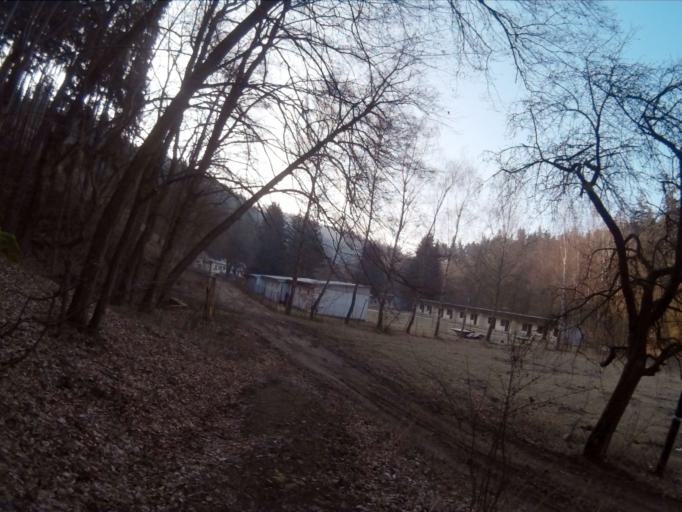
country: CZ
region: Vysocina
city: Namest' nad Oslavou
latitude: 49.1844
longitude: 16.1596
